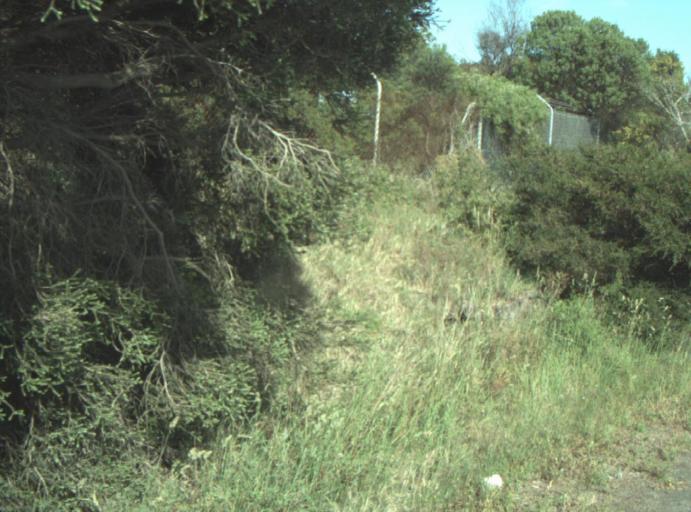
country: AU
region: Victoria
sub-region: Greater Geelong
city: Leopold
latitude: -38.2527
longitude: 144.4814
